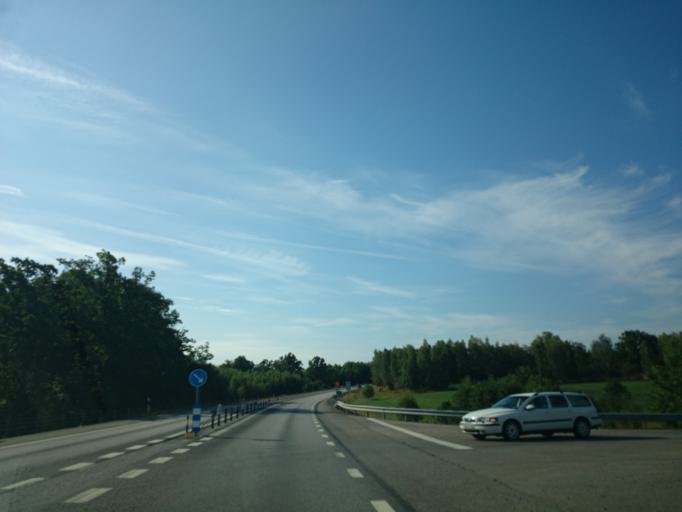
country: SE
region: OEstergoetland
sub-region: Valdemarsviks Kommun
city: Gusum
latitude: 58.3557
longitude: 16.4446
